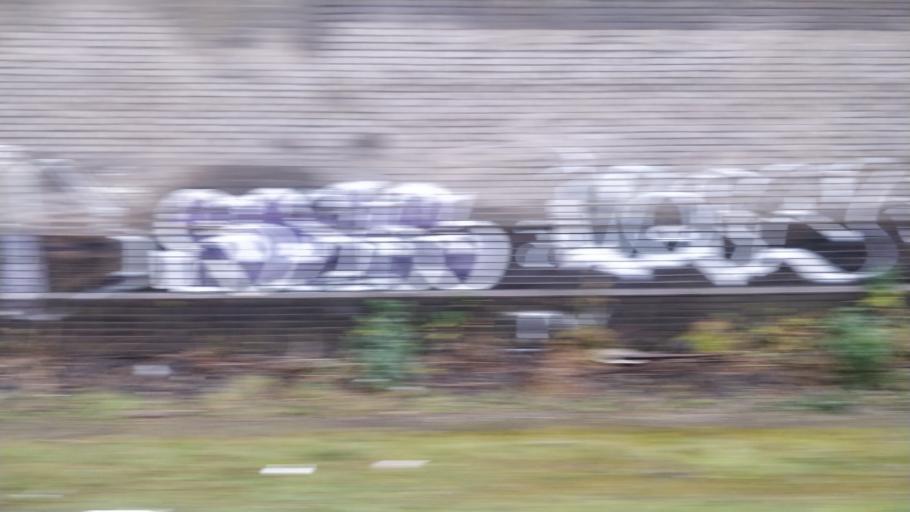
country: GB
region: England
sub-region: City and Borough of Salford
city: Salford
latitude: 53.4935
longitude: -2.2859
